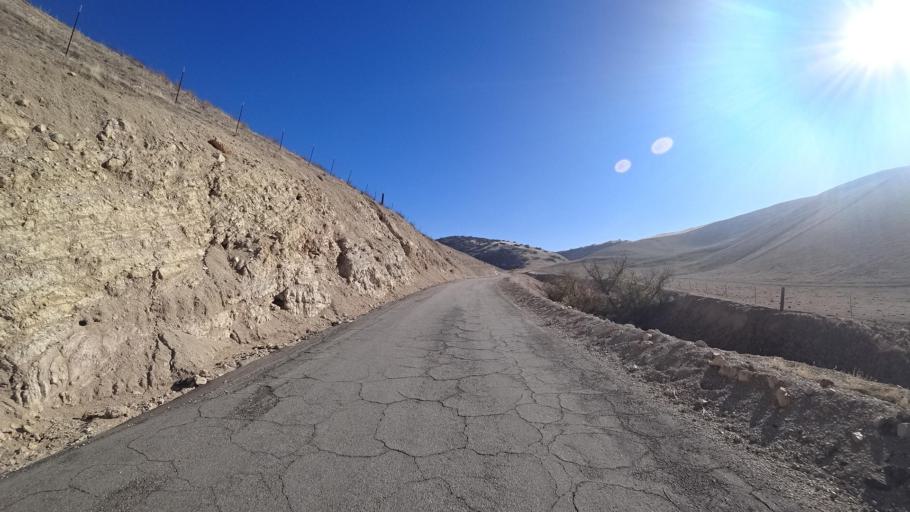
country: US
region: California
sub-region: Kern County
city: Maricopa
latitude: 34.9587
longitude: -119.4099
